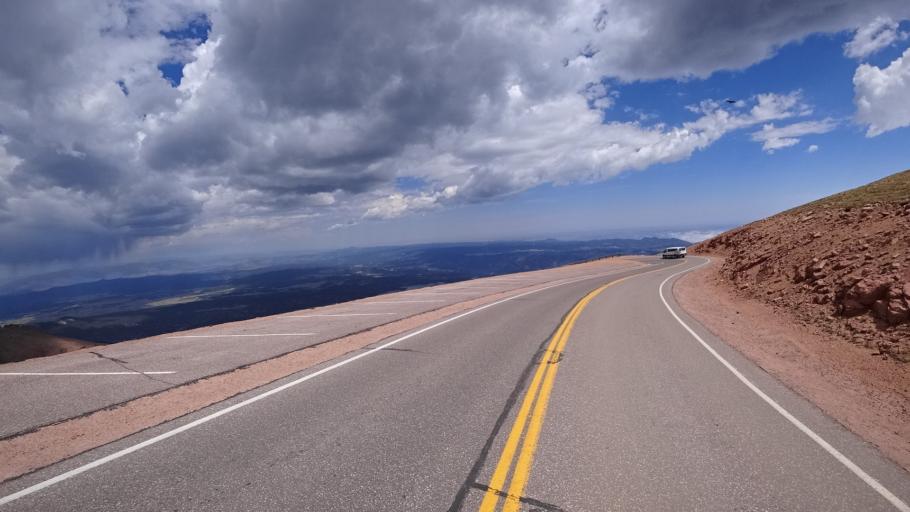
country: US
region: Colorado
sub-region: El Paso County
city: Cascade-Chipita Park
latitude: 38.8647
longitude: -105.0680
